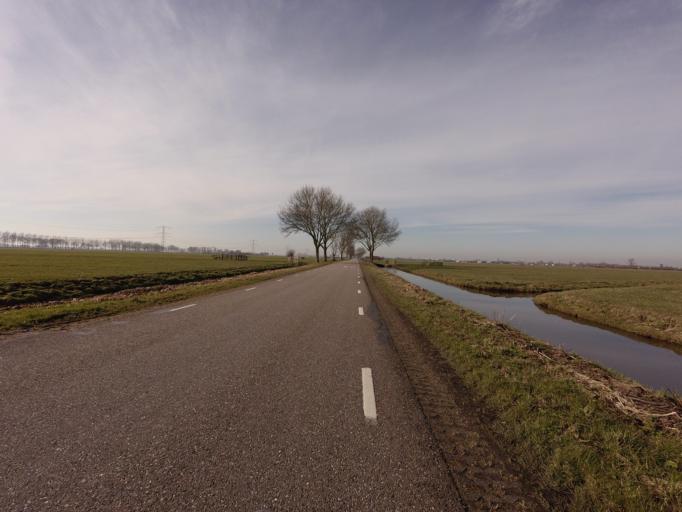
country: NL
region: South Holland
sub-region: Gemeente Sliedrecht
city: Sliedrecht
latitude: 51.8598
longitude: 4.8015
